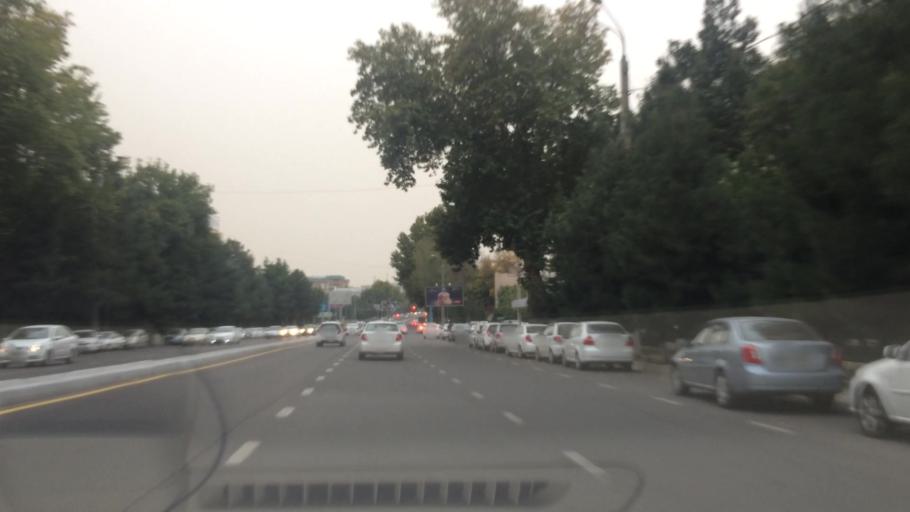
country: UZ
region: Toshkent Shahri
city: Tashkent
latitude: 41.3052
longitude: 69.2822
